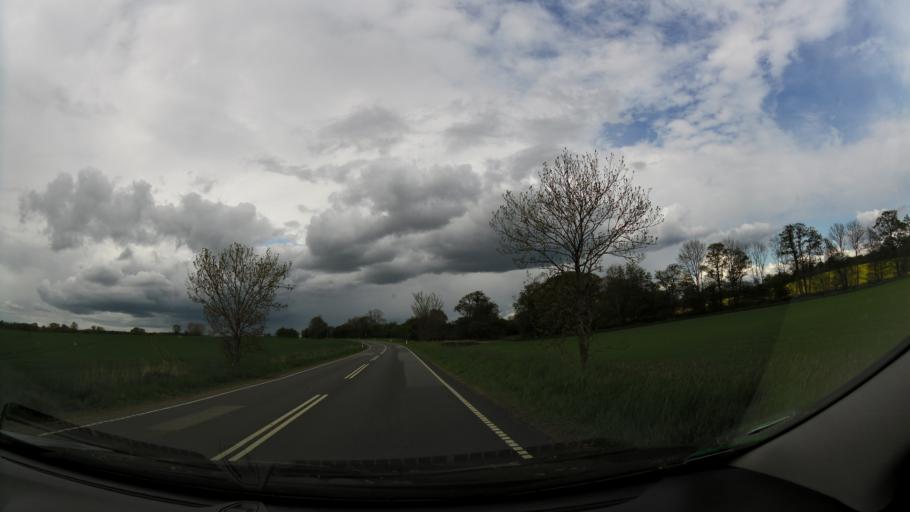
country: DK
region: South Denmark
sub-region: Svendborg Kommune
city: Thuro By
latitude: 55.1437
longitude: 10.7360
